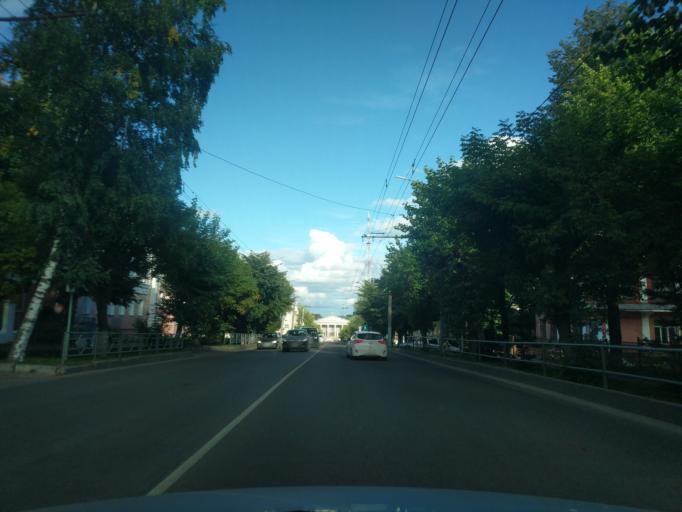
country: RU
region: Kirov
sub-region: Kirovo-Chepetskiy Rayon
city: Kirov
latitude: 58.5941
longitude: 49.6756
